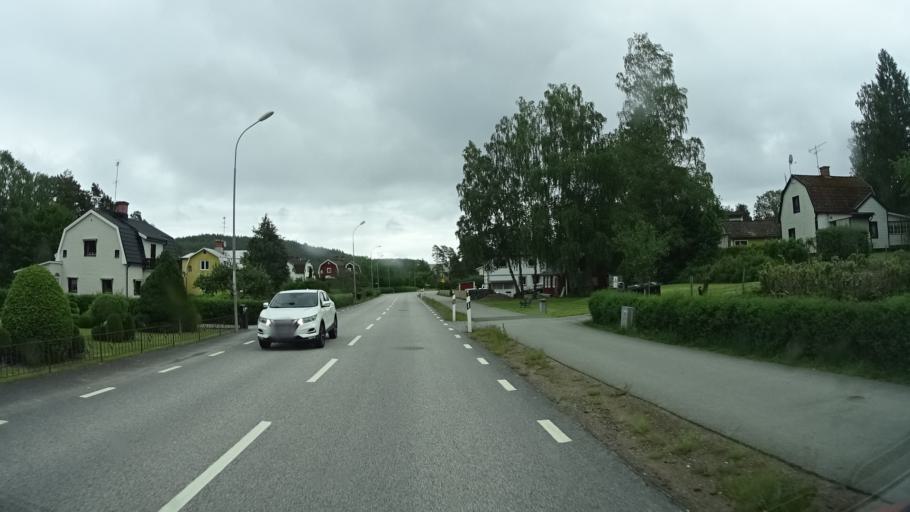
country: SE
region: Kalmar
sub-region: Hultsfreds Kommun
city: Hultsfred
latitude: 57.5435
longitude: 15.7483
